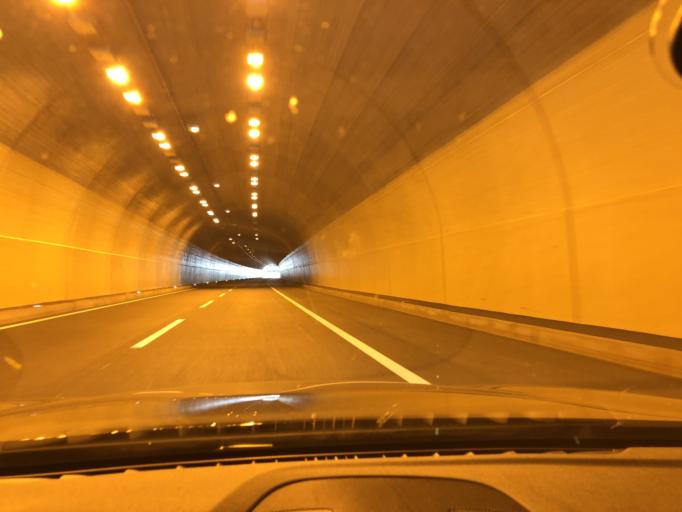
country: AT
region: Tyrol
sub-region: Politischer Bezirk Landeck
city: Flirsch
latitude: 47.1436
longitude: 10.3441
